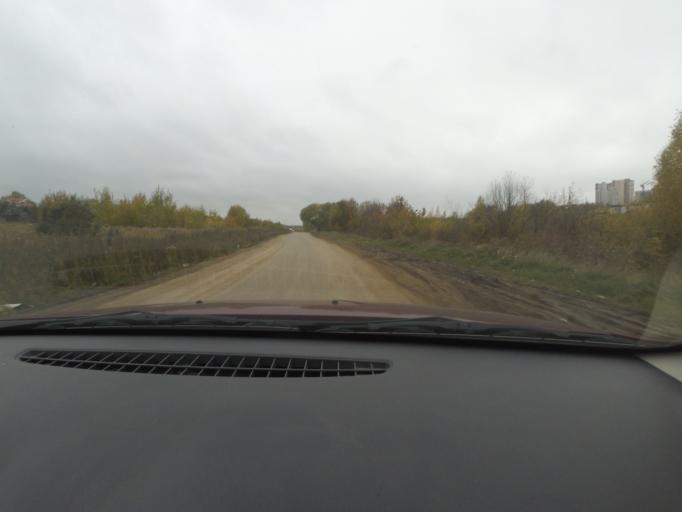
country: RU
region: Nizjnij Novgorod
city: Afonino
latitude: 56.2779
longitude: 44.0428
